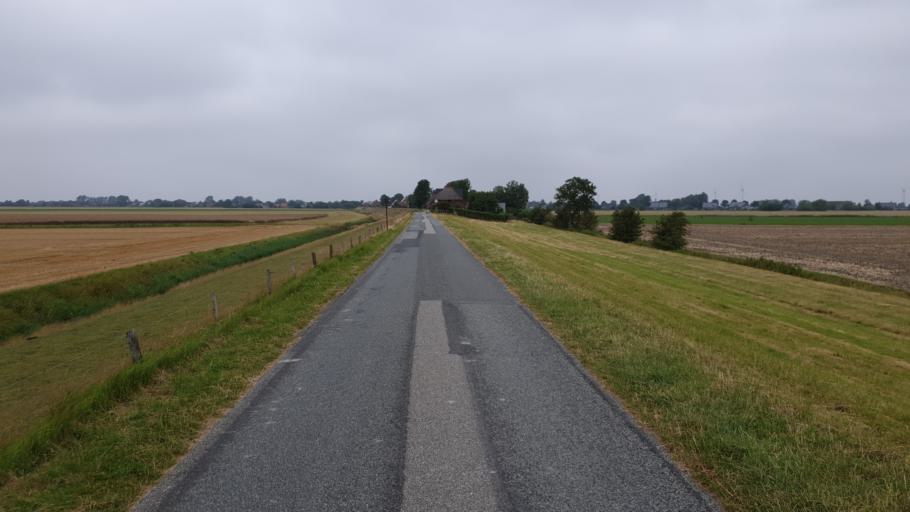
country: DE
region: Schleswig-Holstein
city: Elisabeth-Sophien-Koog
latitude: 54.4806
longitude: 8.8935
